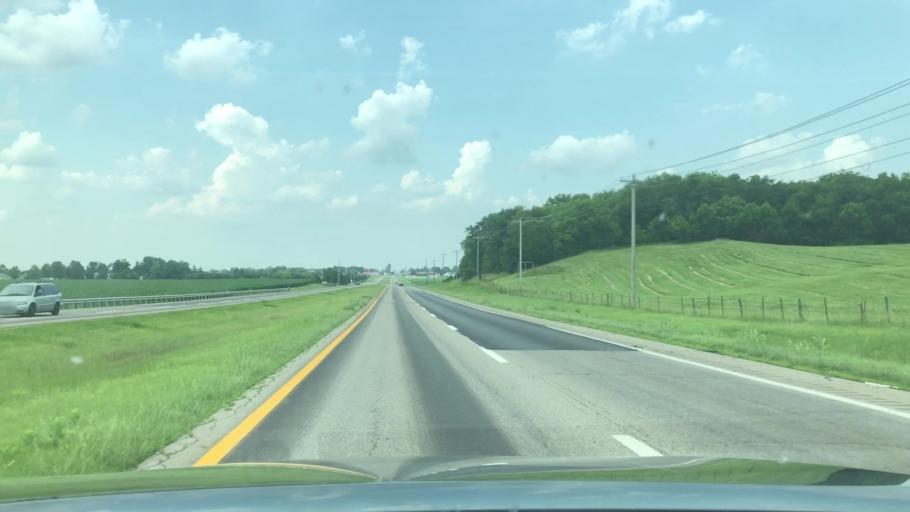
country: US
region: Ohio
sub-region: Pickaway County
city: South Bloomfield
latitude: 39.7018
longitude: -82.9871
